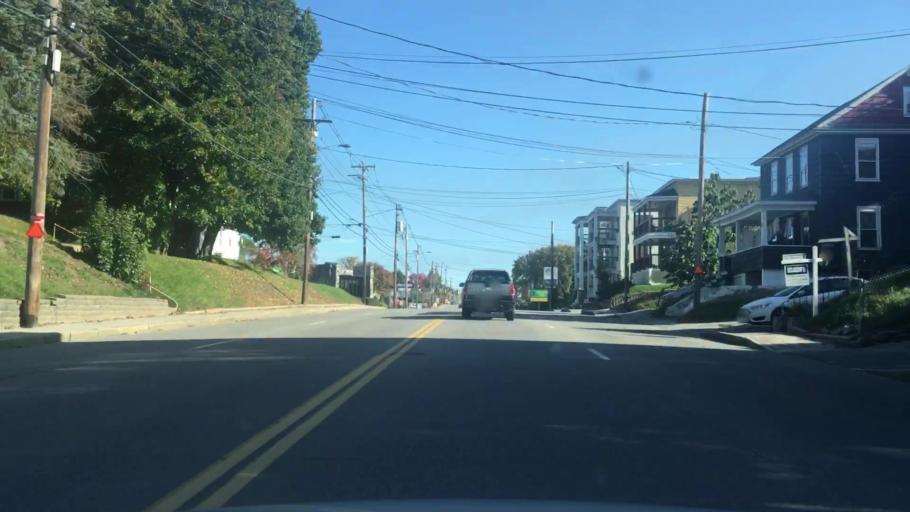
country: US
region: Maine
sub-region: Androscoggin County
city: Lewiston
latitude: 44.0863
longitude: -70.2073
